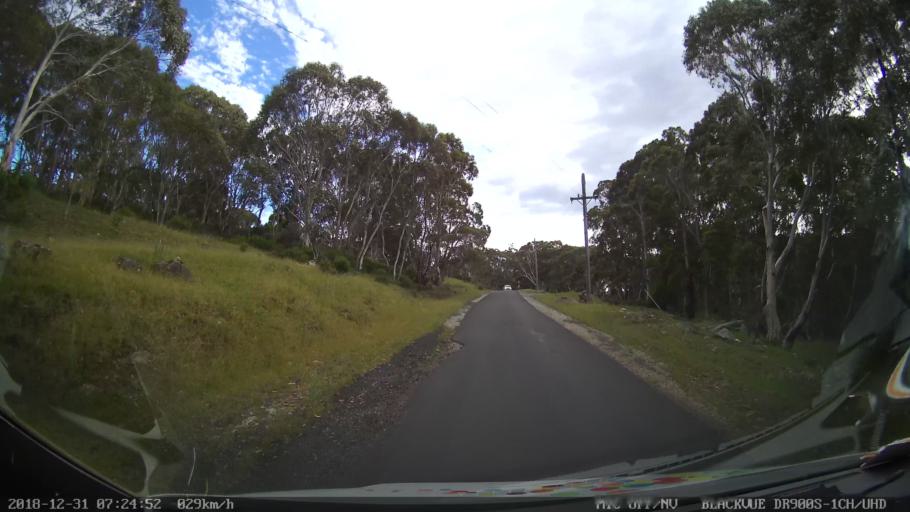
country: AU
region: New South Wales
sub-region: Snowy River
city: Jindabyne
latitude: -36.3222
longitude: 148.4749
